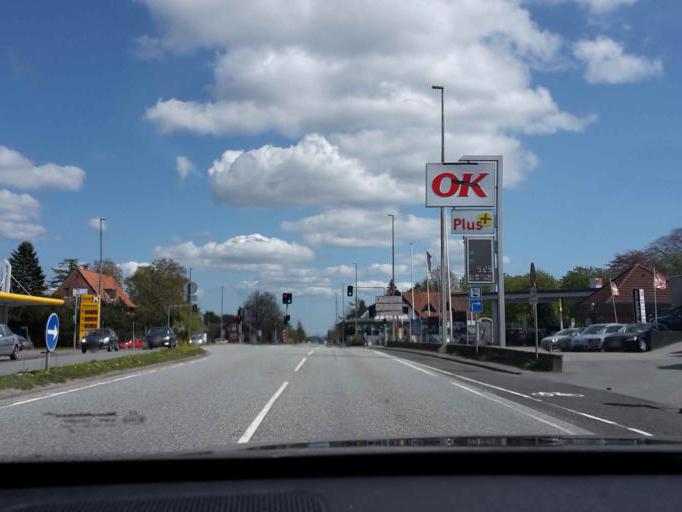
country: DK
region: South Denmark
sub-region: Odense Kommune
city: Bellinge
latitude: 55.3901
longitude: 10.2601
